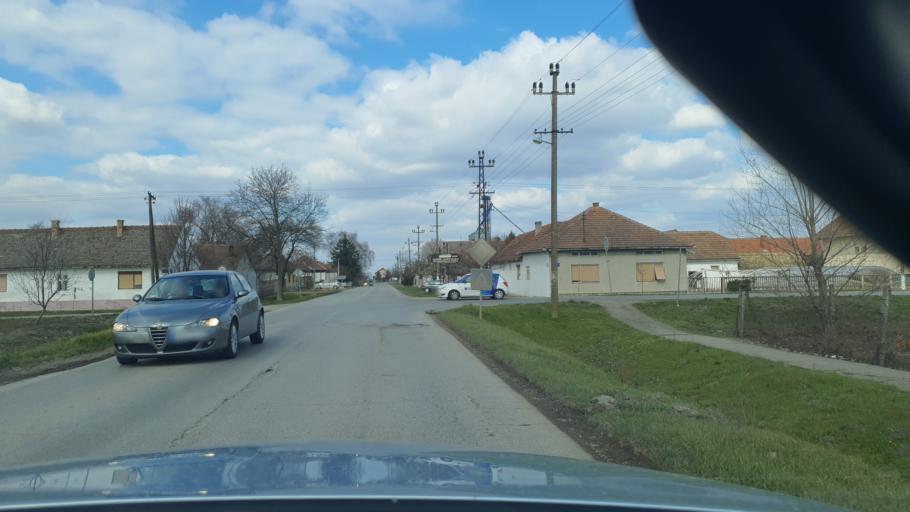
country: RS
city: Maglic
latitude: 45.3939
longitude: 19.4572
